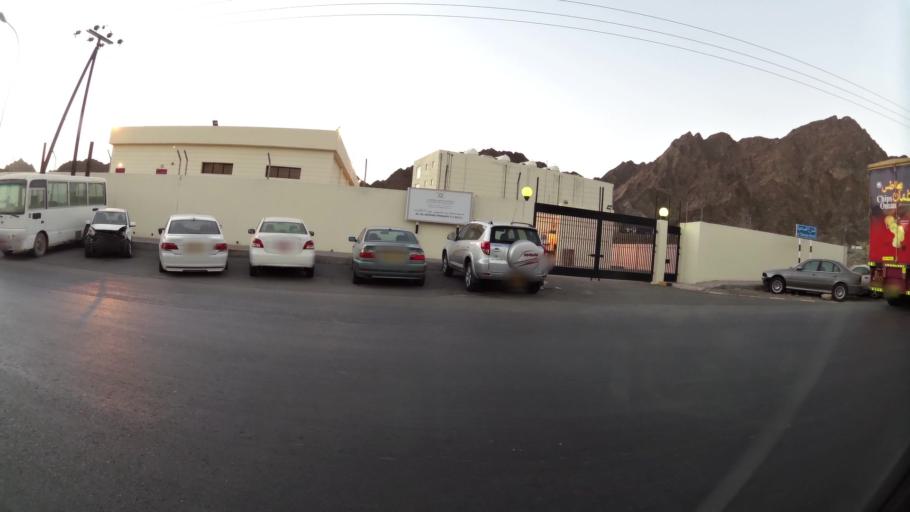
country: OM
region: Muhafazat Masqat
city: Muscat
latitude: 23.5936
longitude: 58.5648
